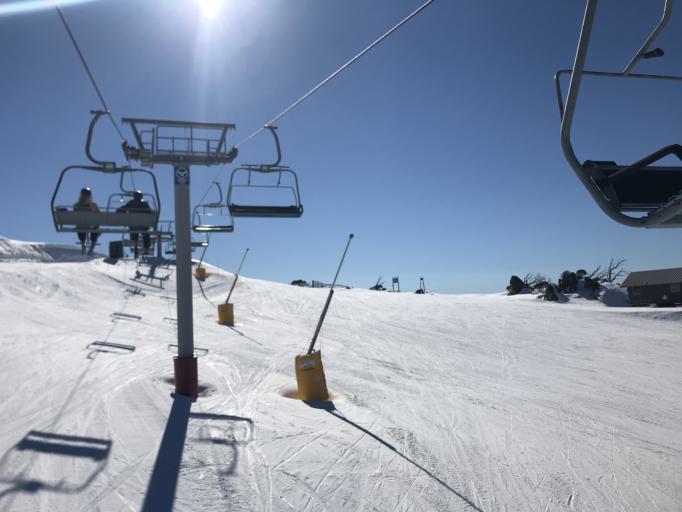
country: AU
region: New South Wales
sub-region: Snowy River
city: Jindabyne
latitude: -36.3780
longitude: 148.3953
